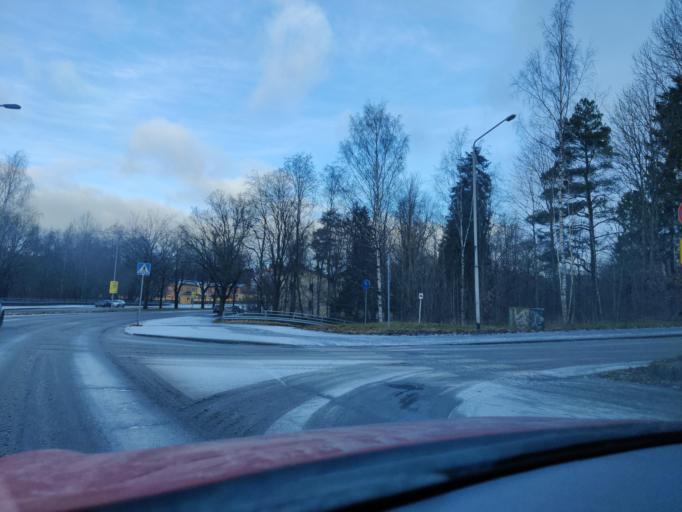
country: FI
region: Pirkanmaa
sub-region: Tampere
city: Nokia
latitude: 61.4757
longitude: 23.5017
